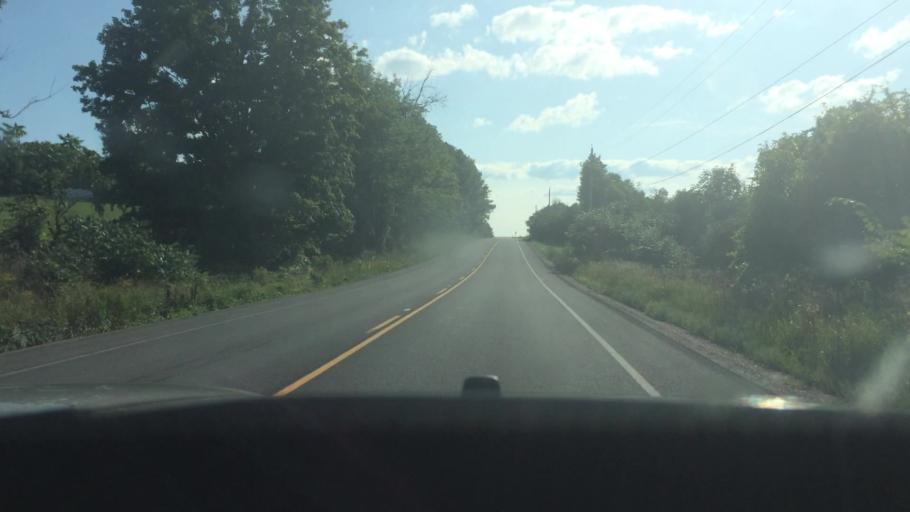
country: US
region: New York
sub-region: Franklin County
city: Malone
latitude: 44.7551
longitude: -74.5503
